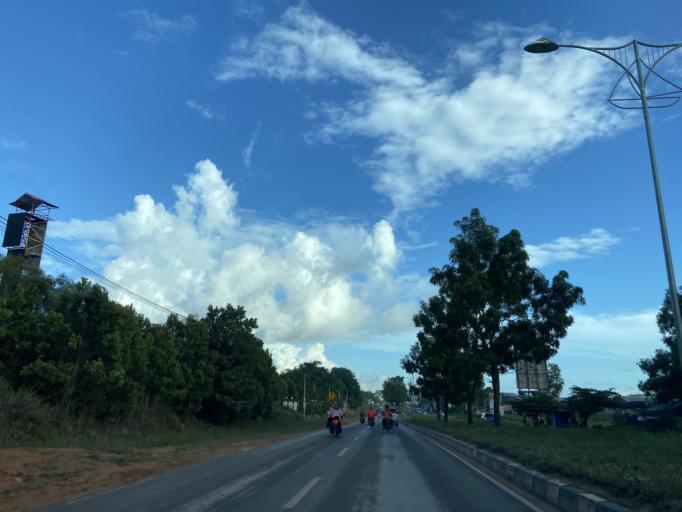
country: SG
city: Singapore
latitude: 1.0300
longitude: 104.0041
